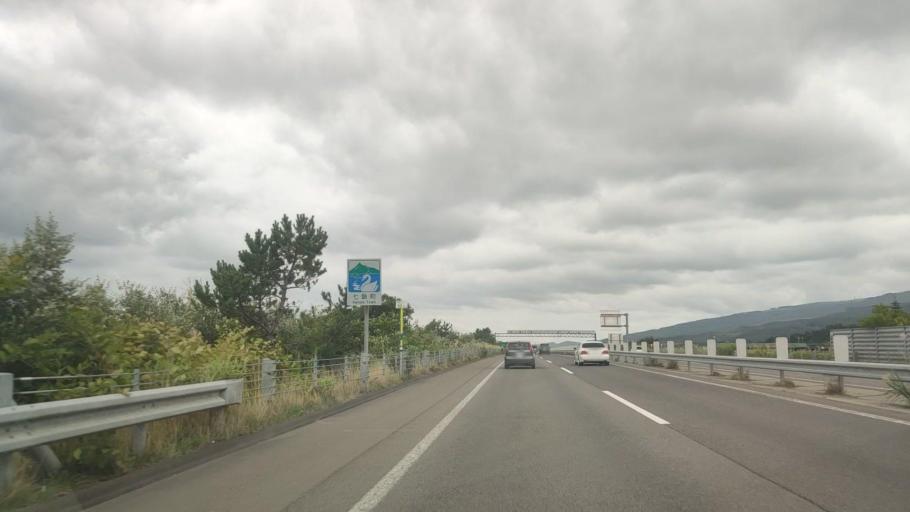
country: JP
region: Hokkaido
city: Nanae
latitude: 41.8594
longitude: 140.7347
